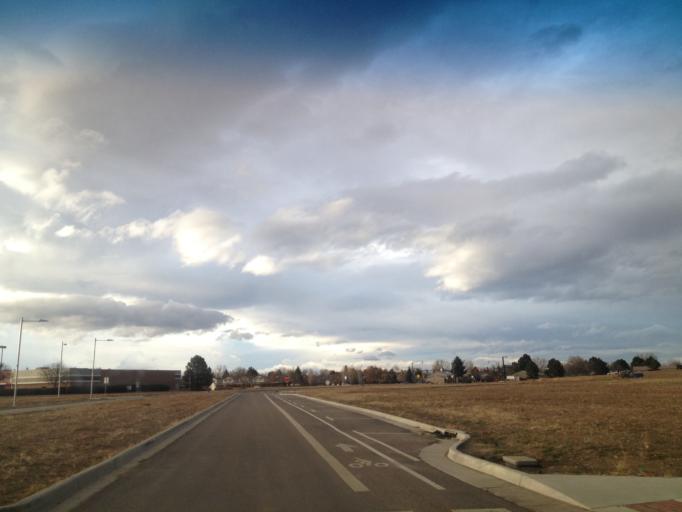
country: US
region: Colorado
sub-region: Adams County
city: Westminster
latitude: 39.8608
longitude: -105.0589
